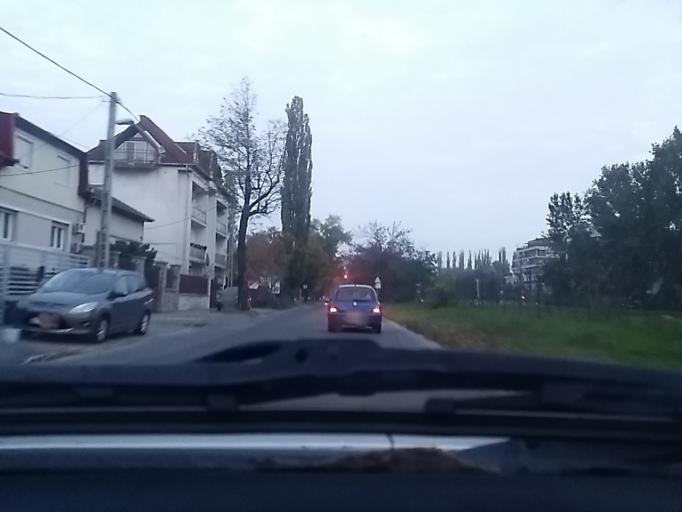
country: HU
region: Budapest
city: Budapest XIV. keruelet
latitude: 47.5234
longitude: 19.1289
